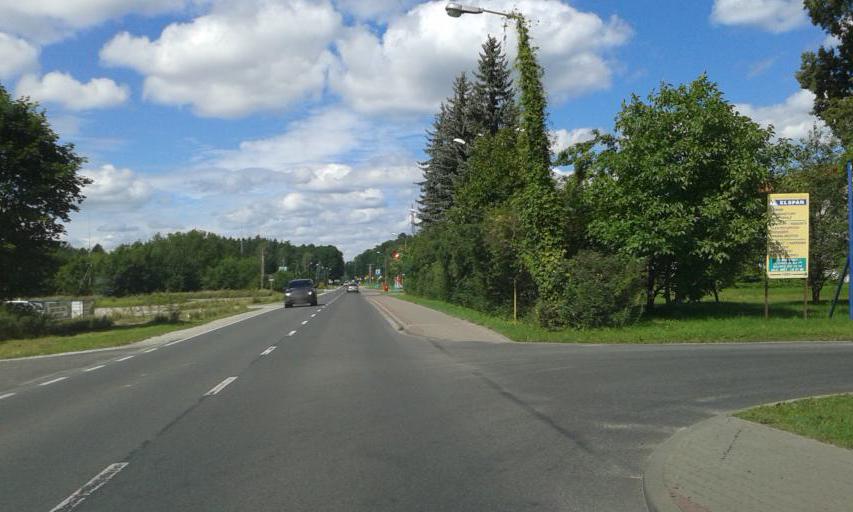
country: PL
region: West Pomeranian Voivodeship
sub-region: Powiat walecki
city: Walcz
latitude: 53.2972
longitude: 16.4563
